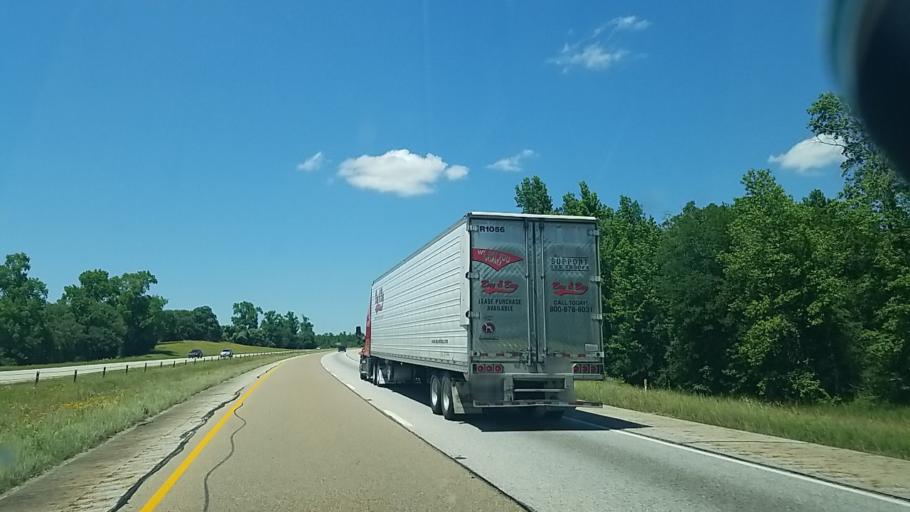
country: US
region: Texas
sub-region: Leon County
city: Centerville
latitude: 31.2090
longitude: -95.9965
